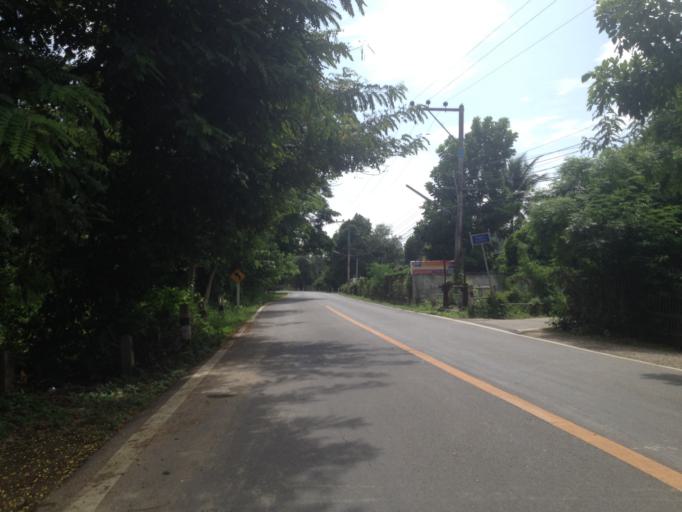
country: TH
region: Chiang Mai
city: Hang Dong
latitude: 18.6756
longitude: 98.9725
